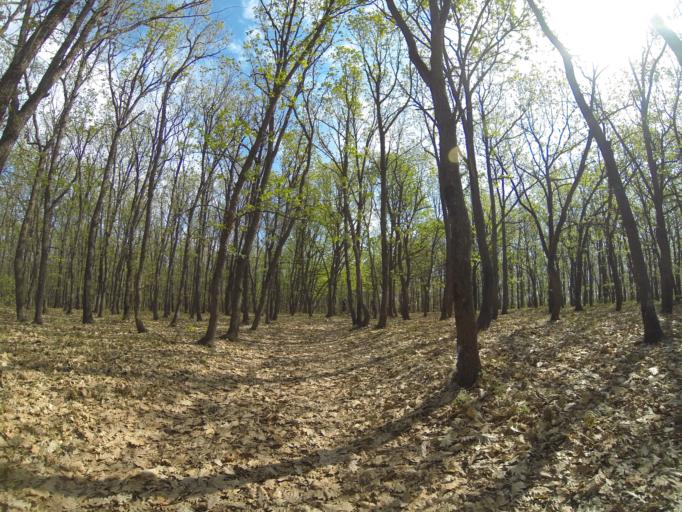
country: RO
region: Dolj
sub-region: Comuna Bradesti
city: Bradesti
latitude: 44.5231
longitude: 23.6140
